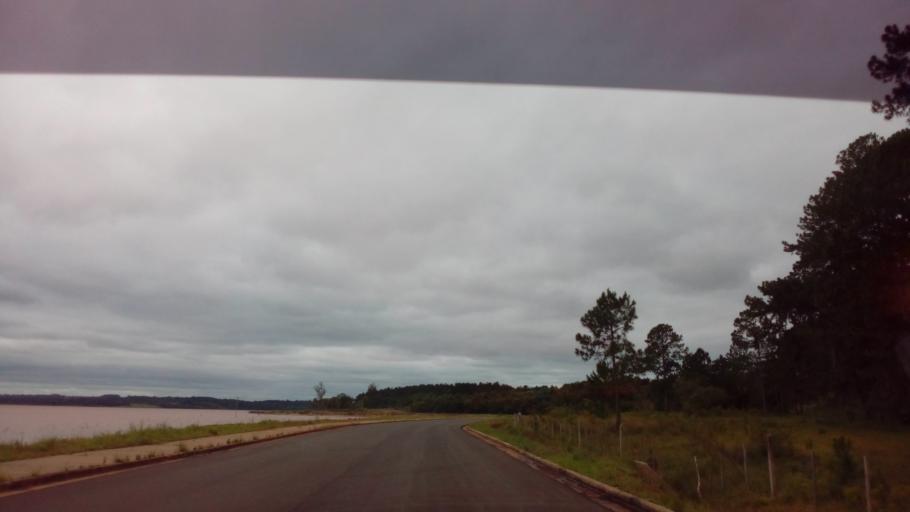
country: AR
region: Misiones
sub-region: Departamento de Candelaria
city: Candelaria
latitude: -27.4555
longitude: -55.7887
